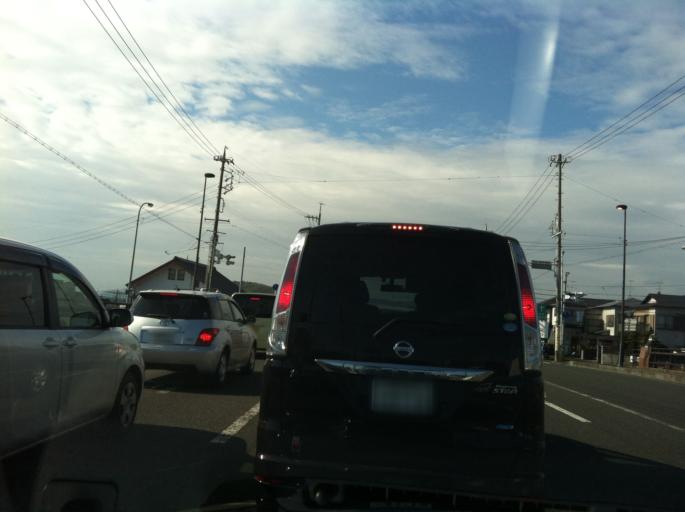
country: JP
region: Shizuoka
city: Shizuoka-shi
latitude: 35.0033
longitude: 138.4226
